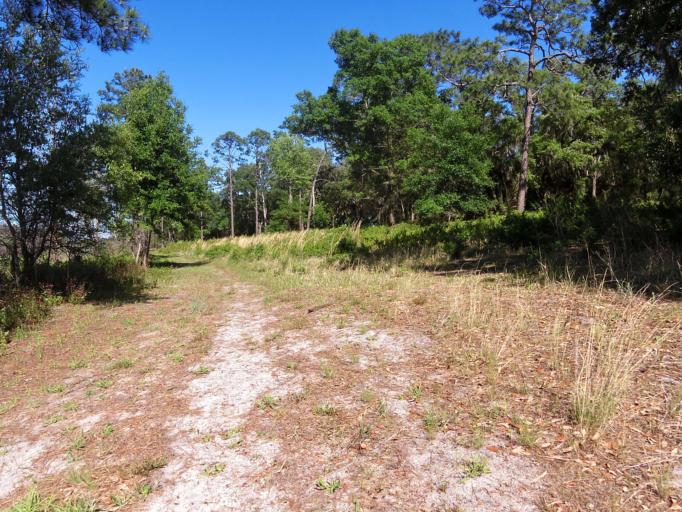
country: US
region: Florida
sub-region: Clay County
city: Keystone Heights
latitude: 29.8241
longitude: -81.9471
